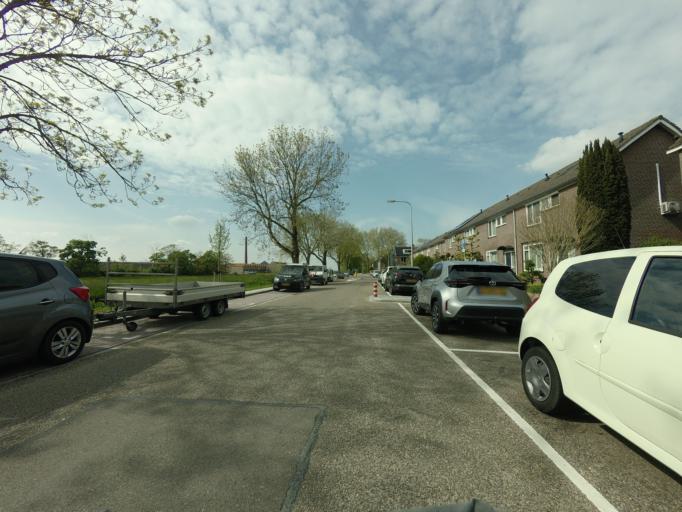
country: NL
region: Utrecht
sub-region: Gemeente Oudewater
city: Oudewater
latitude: 52.0258
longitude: 4.8608
